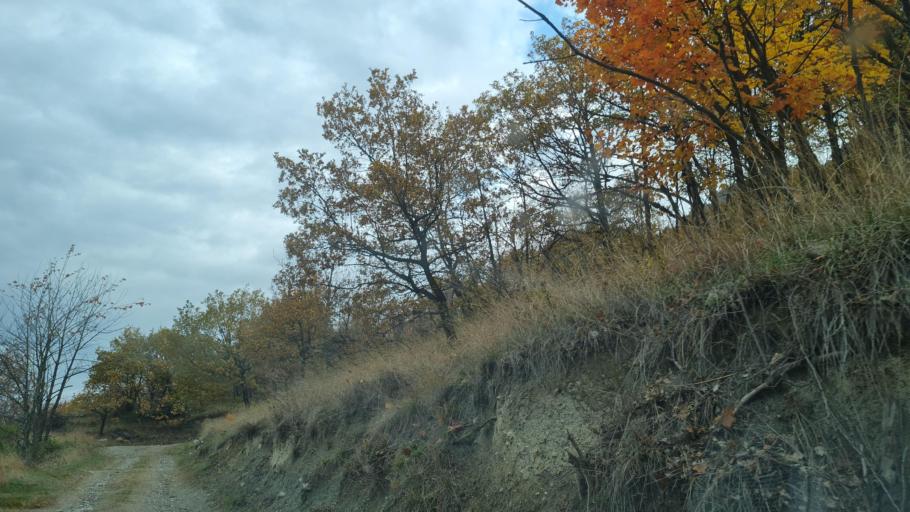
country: IT
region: Piedmont
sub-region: Provincia di Torino
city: Bussoleno
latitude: 45.1528
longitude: 7.1334
